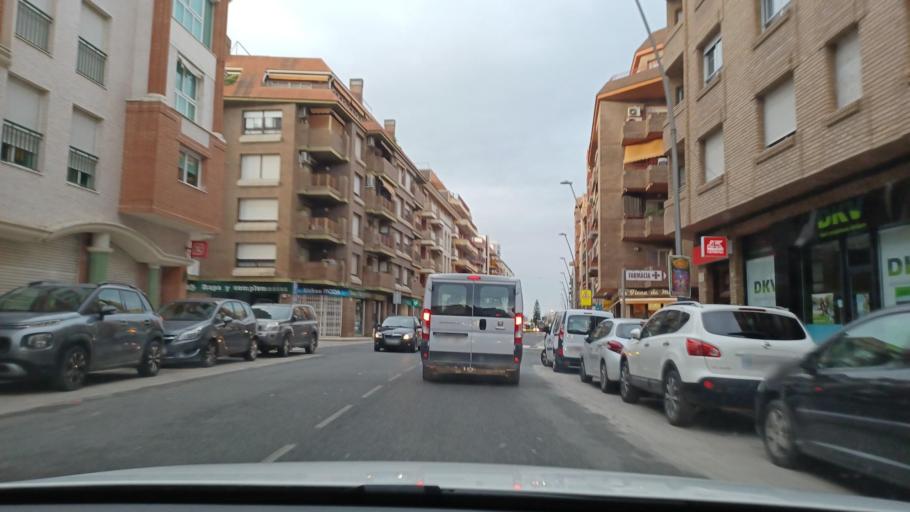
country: ES
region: Catalonia
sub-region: Provincia de Tarragona
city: Tortosa
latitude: 40.8050
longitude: 0.5206
